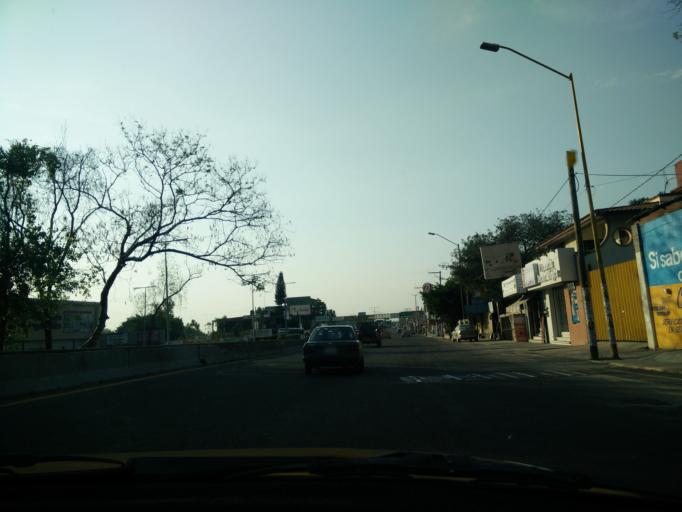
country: MX
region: Oaxaca
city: Oaxaca de Juarez
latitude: 17.0814
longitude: -96.7430
